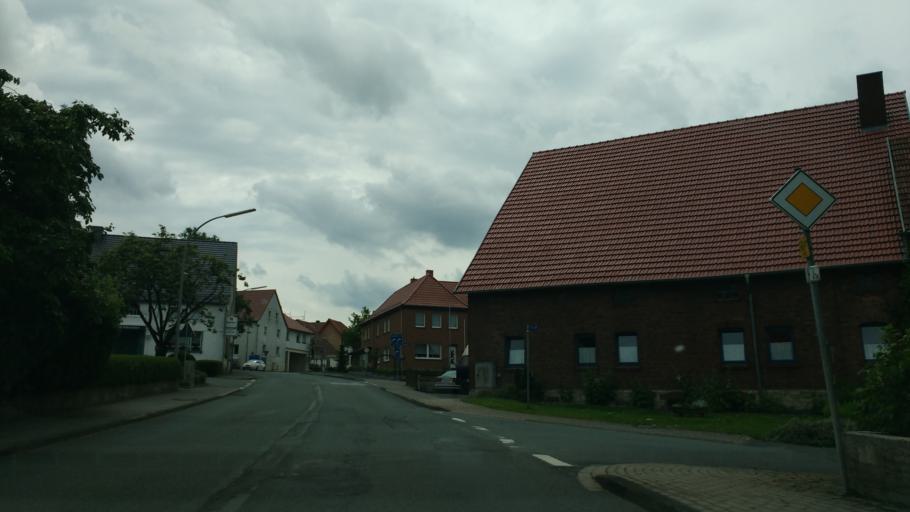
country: DE
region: North Rhine-Westphalia
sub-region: Regierungsbezirk Detmold
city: Wunnenberg
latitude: 51.5651
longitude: 8.7270
